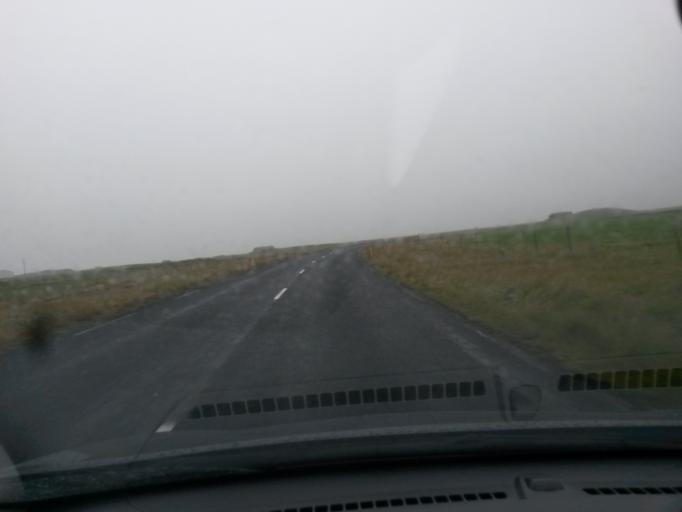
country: IS
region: South
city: Vestmannaeyjar
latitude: 63.4324
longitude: -19.1868
